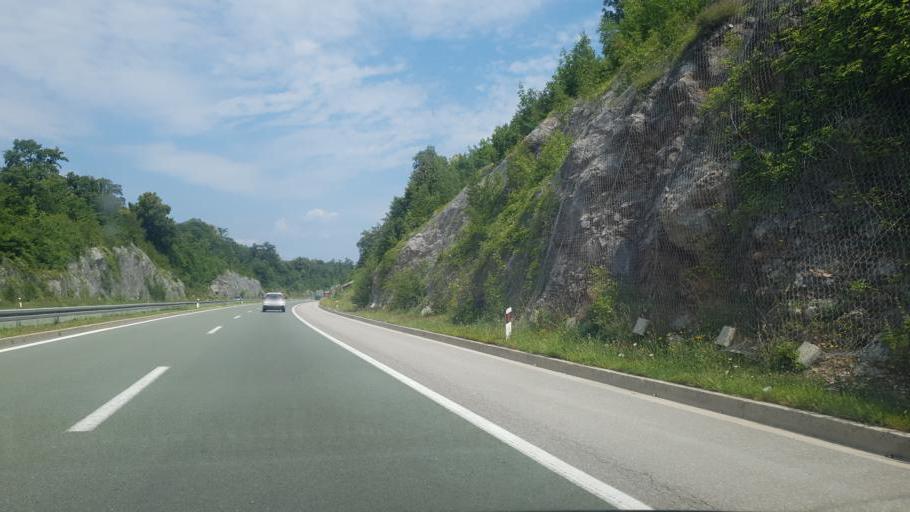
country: HR
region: Primorsko-Goranska
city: Matulji
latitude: 45.3842
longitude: 14.3032
